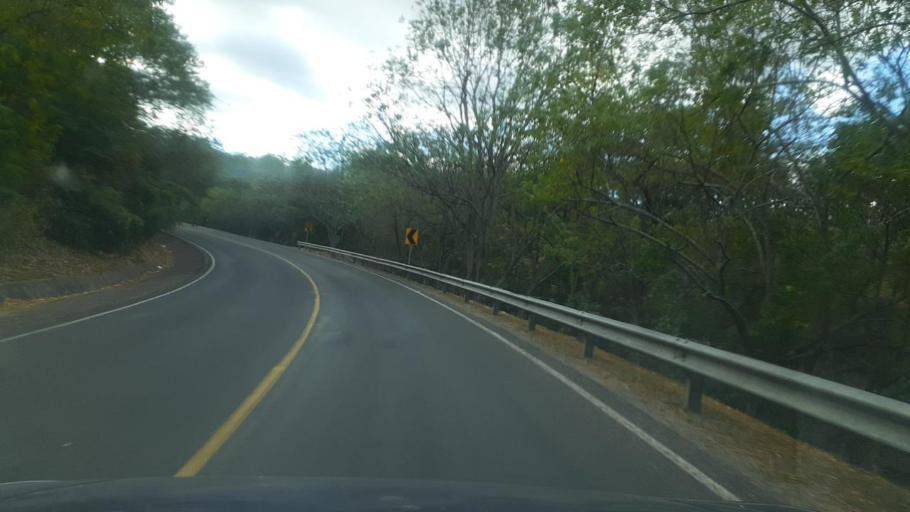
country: NI
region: Madriz
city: Somoto
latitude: 13.5061
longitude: -86.5619
